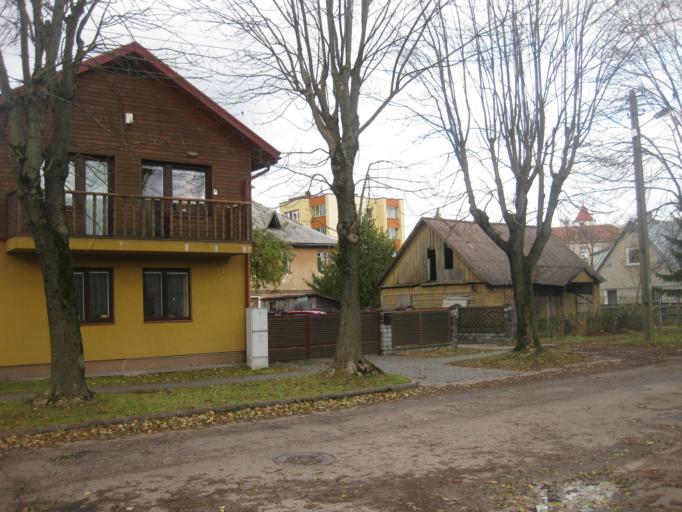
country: LT
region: Kauno apskritis
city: Dainava (Kaunas)
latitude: 54.9043
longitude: 23.9446
